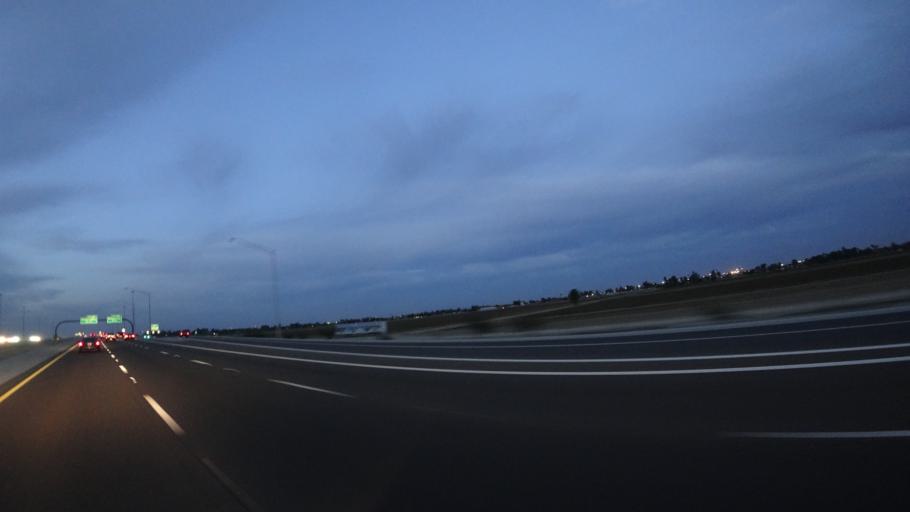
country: US
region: Arizona
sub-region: Maricopa County
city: Citrus Park
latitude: 33.5329
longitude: -112.4181
